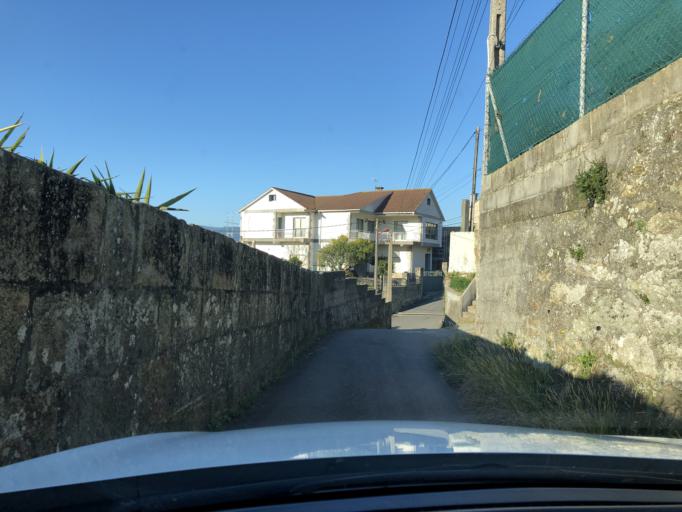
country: ES
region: Galicia
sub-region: Provincia de Pontevedra
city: Marin
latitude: 42.3921
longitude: -8.6906
